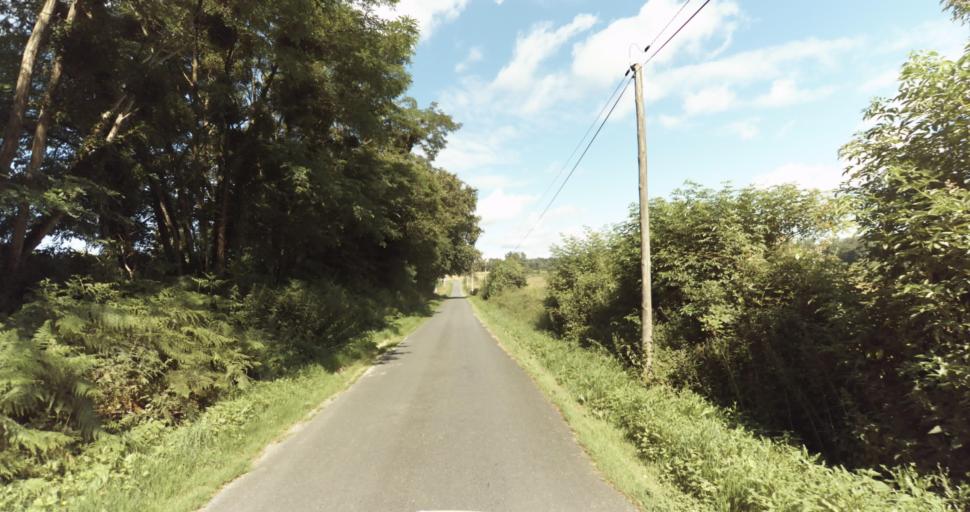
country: FR
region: Aquitaine
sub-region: Departement de la Gironde
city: Bazas
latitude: 44.4488
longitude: -0.2033
